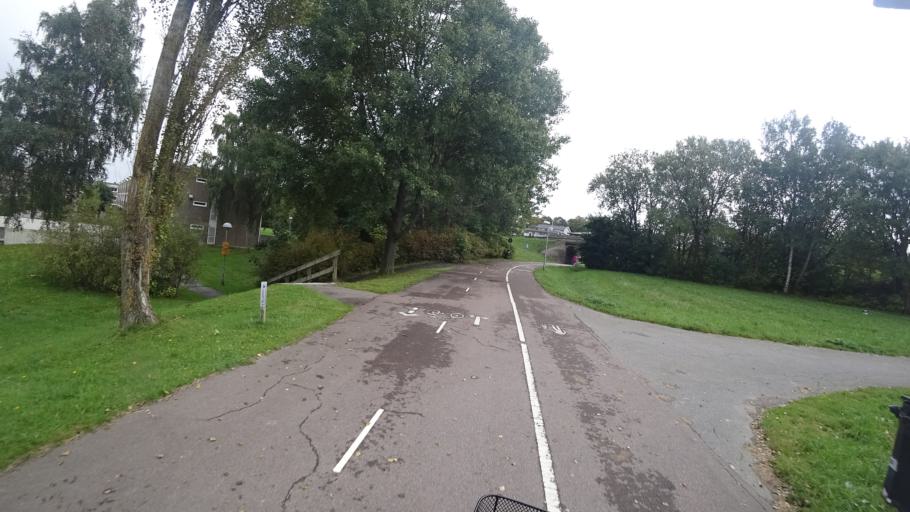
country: SE
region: Vaestra Goetaland
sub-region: Goteborg
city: Majorna
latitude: 57.6369
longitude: 11.9424
